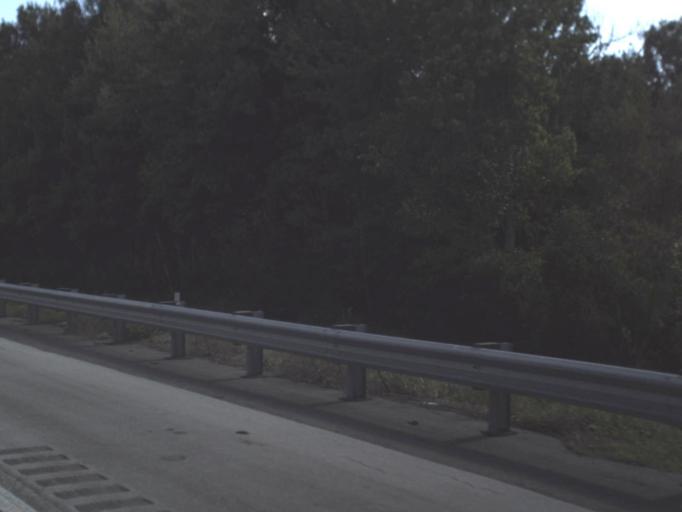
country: US
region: Florida
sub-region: Osceola County
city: Saint Cloud
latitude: 28.0325
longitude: -81.1959
